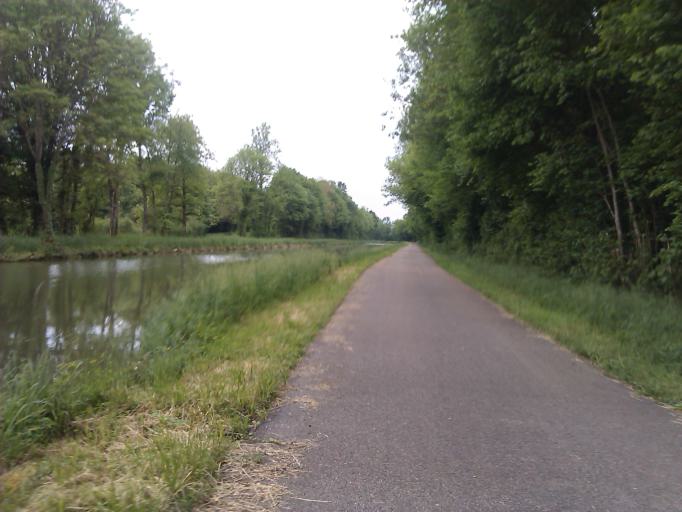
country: FR
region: Franche-Comte
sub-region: Departement du Jura
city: Damparis
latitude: 47.0794
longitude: 5.3604
